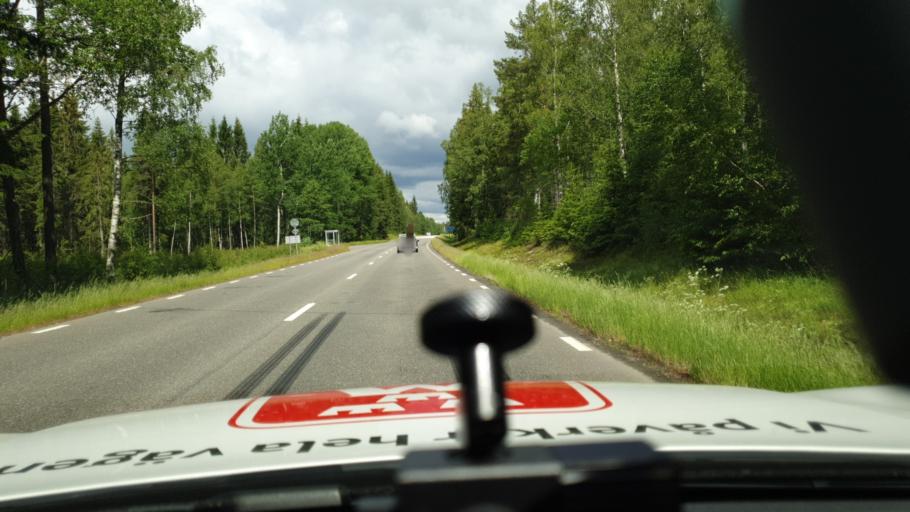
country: SE
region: Vaestra Goetaland
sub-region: Karlsborgs Kommun
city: Molltorp
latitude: 58.6052
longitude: 14.3946
